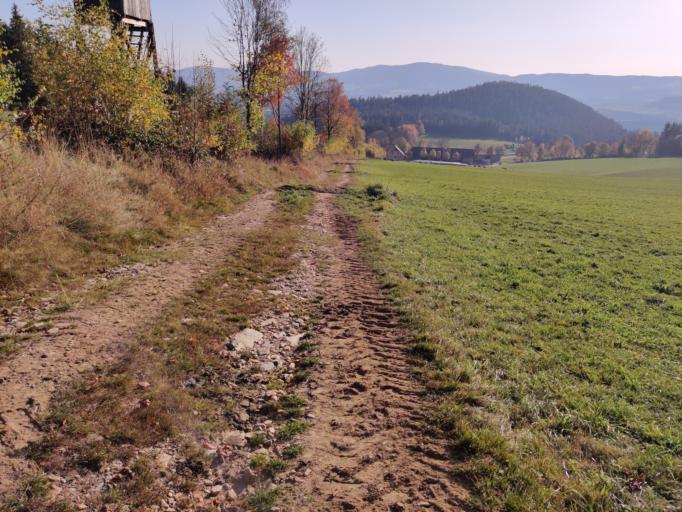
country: AT
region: Styria
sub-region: Politischer Bezirk Hartberg-Fuerstenfeld
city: Sankt Jakob im Walde
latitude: 47.4695
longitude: 15.8108
